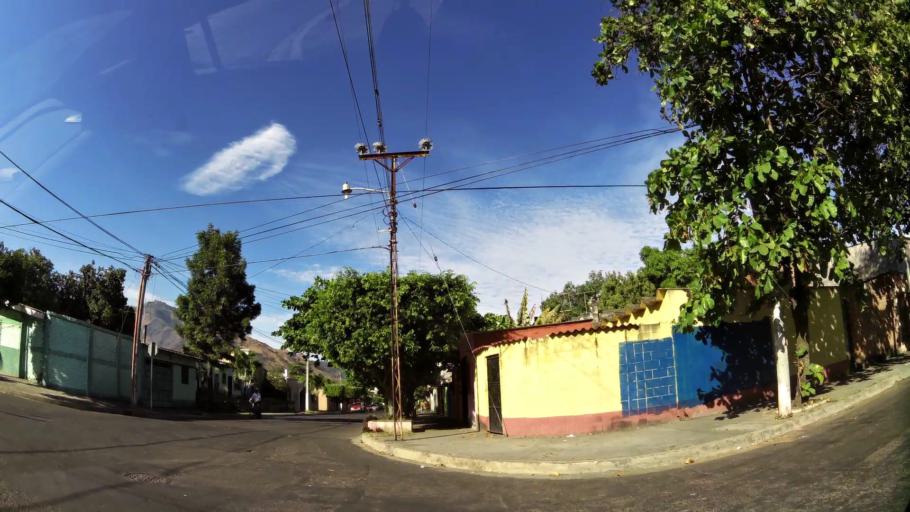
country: SV
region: Santa Ana
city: Santa Ana
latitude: 13.9992
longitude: -89.5585
